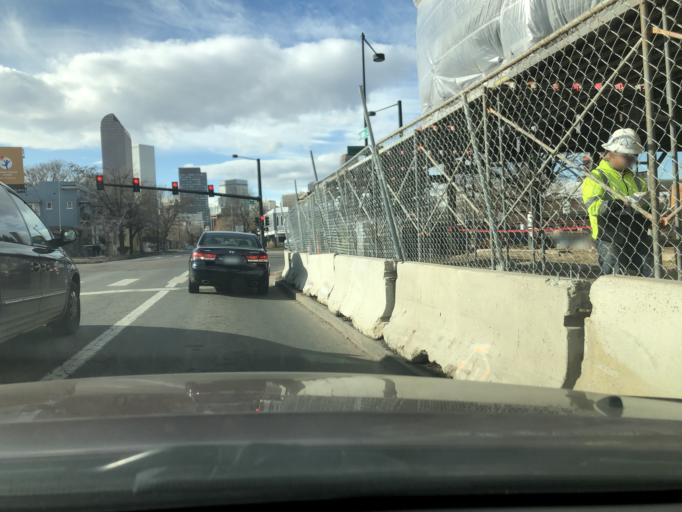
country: US
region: Colorado
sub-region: Denver County
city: Denver
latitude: 39.7449
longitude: -104.9743
